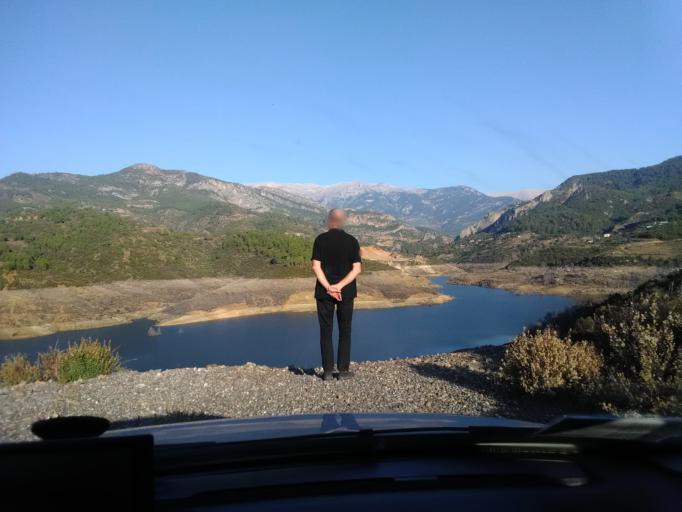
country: TR
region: Antalya
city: Gazipasa
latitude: 36.3141
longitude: 32.3917
